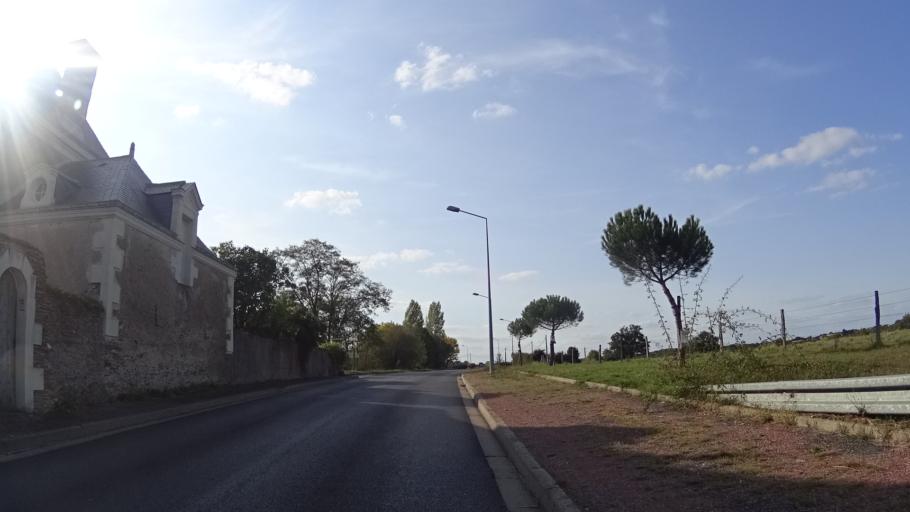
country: FR
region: Pays de la Loire
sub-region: Departement de Maine-et-Loire
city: Bouchemaine
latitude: 47.4097
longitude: -0.6213
